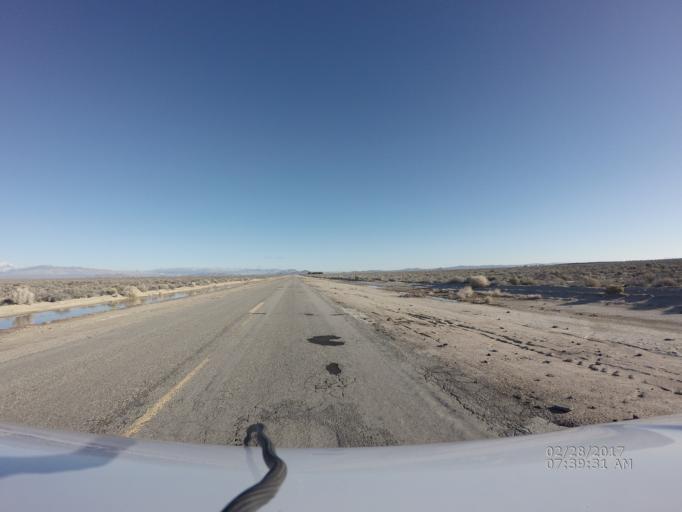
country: US
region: California
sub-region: Los Angeles County
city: Lancaster
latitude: 34.7685
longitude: -118.1845
